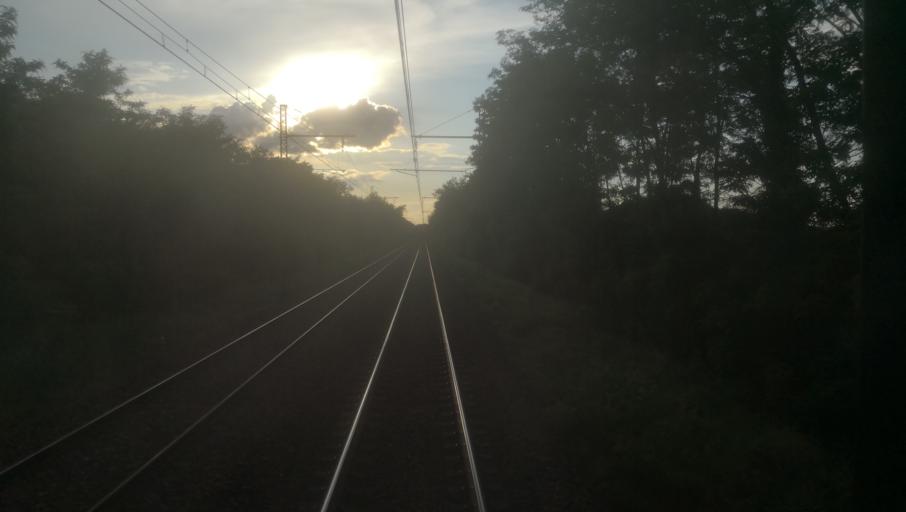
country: FR
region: Centre
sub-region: Departement de l'Indre
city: Le Pechereau
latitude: 46.4982
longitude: 1.5197
